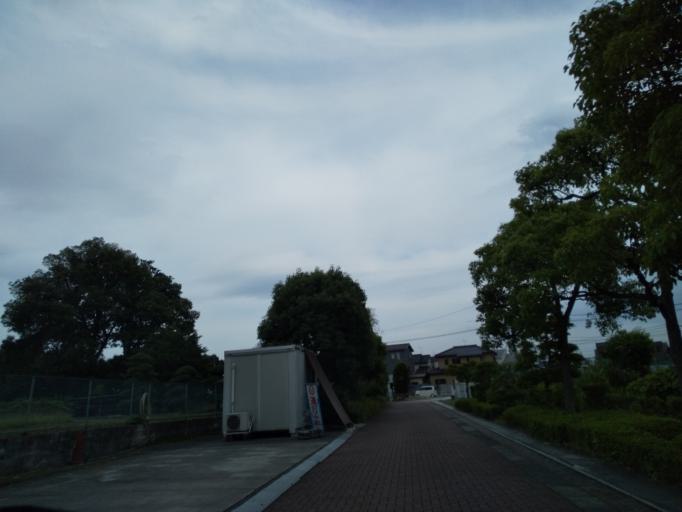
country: JP
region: Saitama
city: Kasukabe
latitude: 35.9932
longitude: 139.8120
